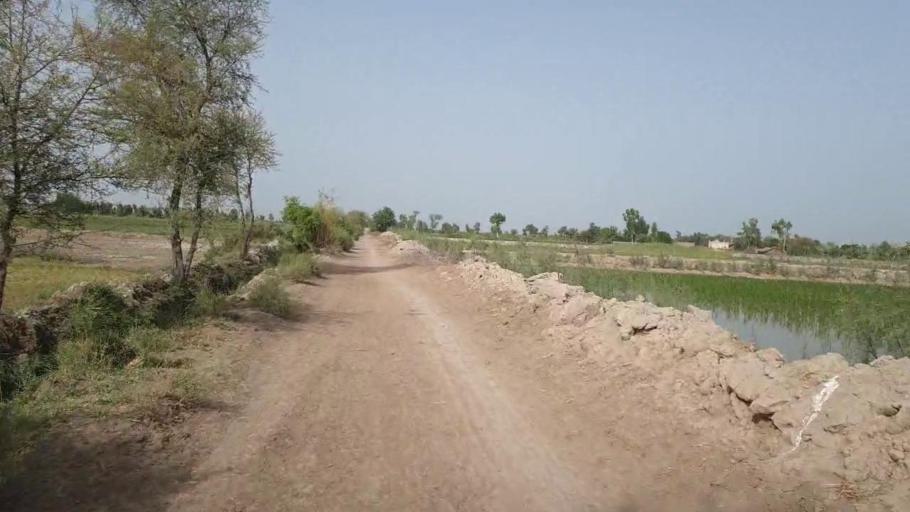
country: PK
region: Sindh
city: Daur
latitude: 26.4340
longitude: 68.1575
